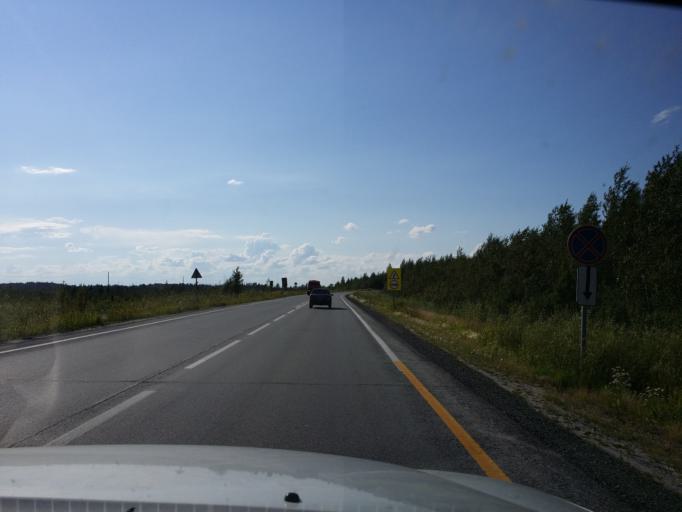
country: RU
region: Khanty-Mansiyskiy Avtonomnyy Okrug
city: Lokosovo
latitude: 61.3948
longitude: 74.8704
